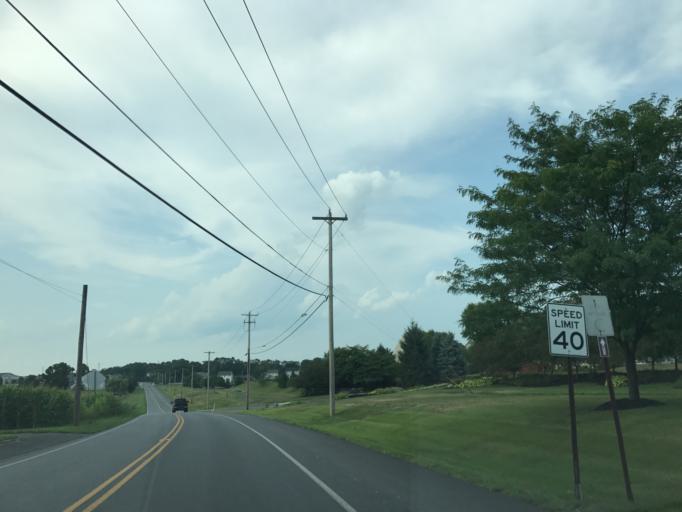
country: US
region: Pennsylvania
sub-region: Lancaster County
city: Mount Joy
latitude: 40.1079
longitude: -76.5324
